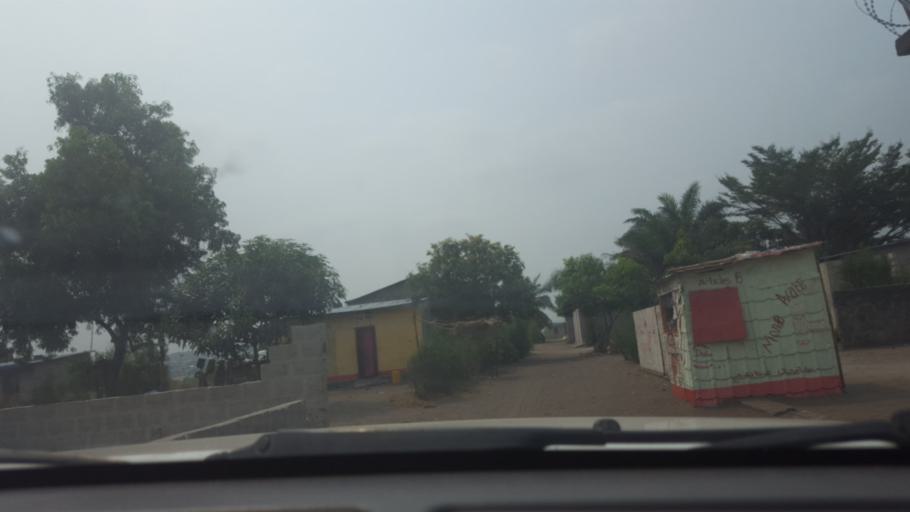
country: CD
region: Kinshasa
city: Masina
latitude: -4.3586
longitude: 15.5118
